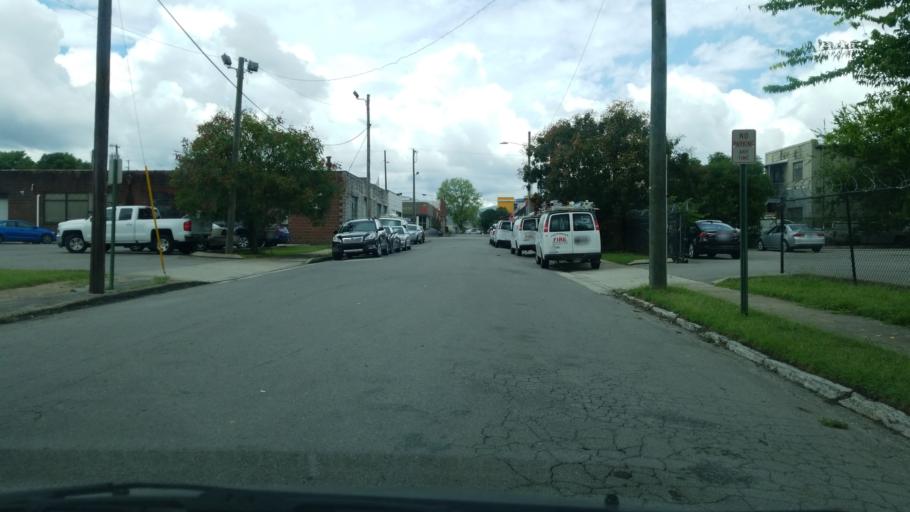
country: US
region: Tennessee
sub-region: Hamilton County
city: Chattanooga
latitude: 35.0339
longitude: -85.3122
